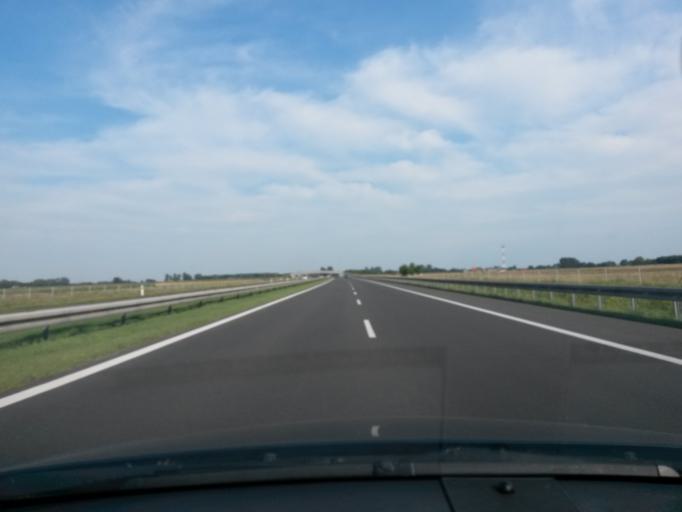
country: PL
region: Greater Poland Voivodeship
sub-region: Powiat wrzesinski
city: Pyzdry
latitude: 52.2711
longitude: 17.7186
